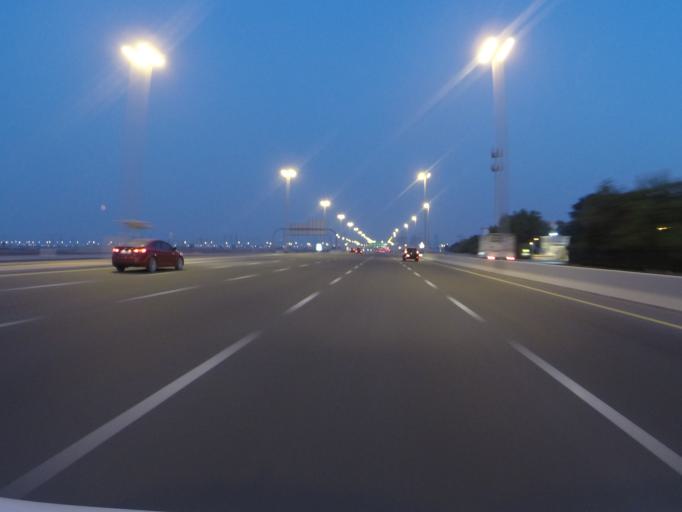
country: AE
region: Dubai
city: Dubai
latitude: 25.0746
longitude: 55.1847
